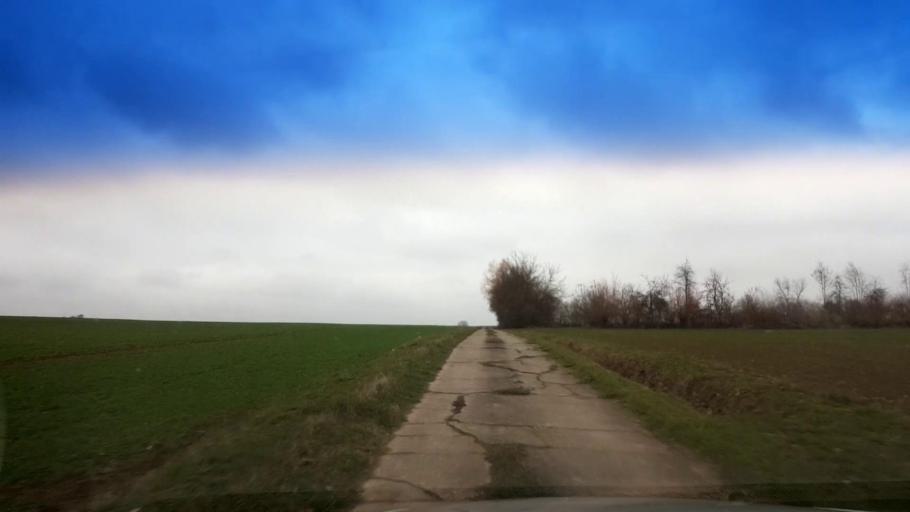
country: DE
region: Bavaria
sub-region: Upper Franconia
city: Zapfendorf
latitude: 49.9814
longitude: 10.9533
